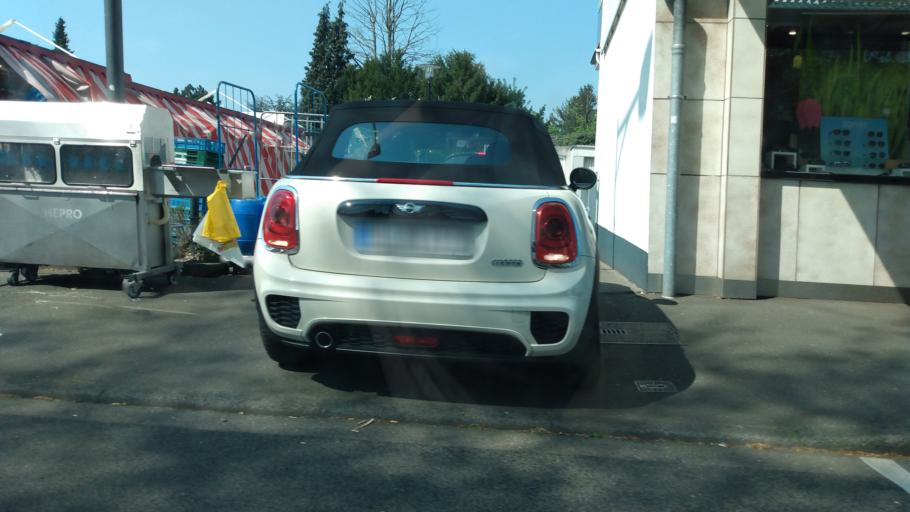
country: DE
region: North Rhine-Westphalia
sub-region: Regierungsbezirk Koln
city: Odenthal
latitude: 51.0156
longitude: 7.0804
